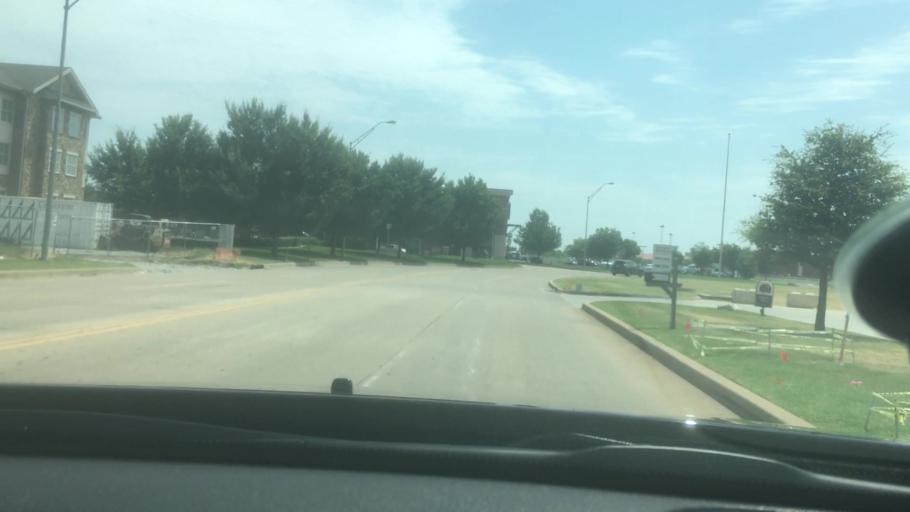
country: US
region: Oklahoma
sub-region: Oklahoma County
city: Bethany
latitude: 35.4628
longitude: -97.6360
